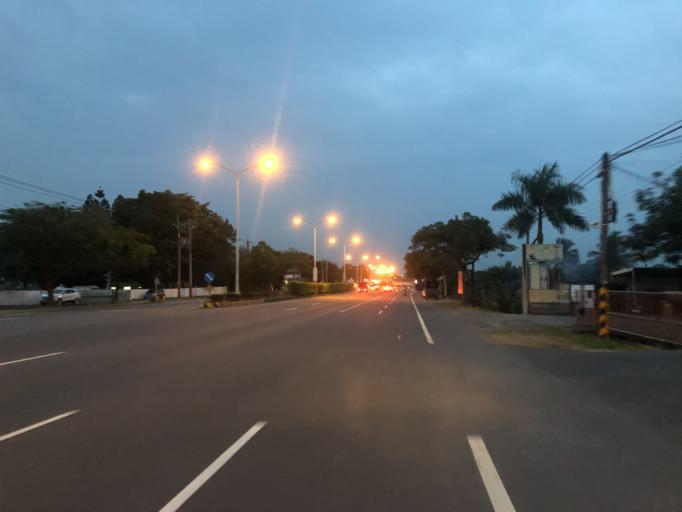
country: TW
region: Taiwan
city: Yujing
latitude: 23.1470
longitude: 120.3304
